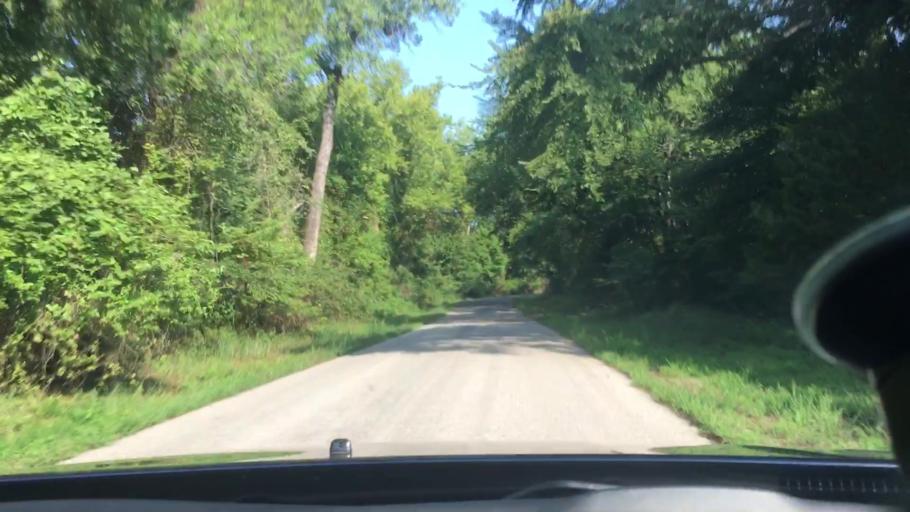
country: US
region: Oklahoma
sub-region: Johnston County
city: Tishomingo
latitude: 34.2024
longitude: -96.6678
